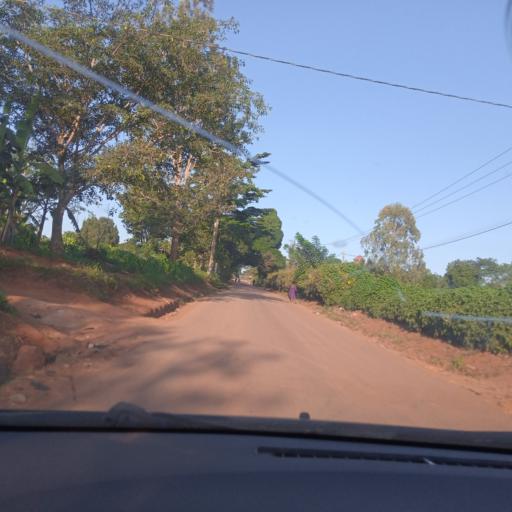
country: UG
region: Central Region
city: Masaka
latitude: -0.3299
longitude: 31.7555
